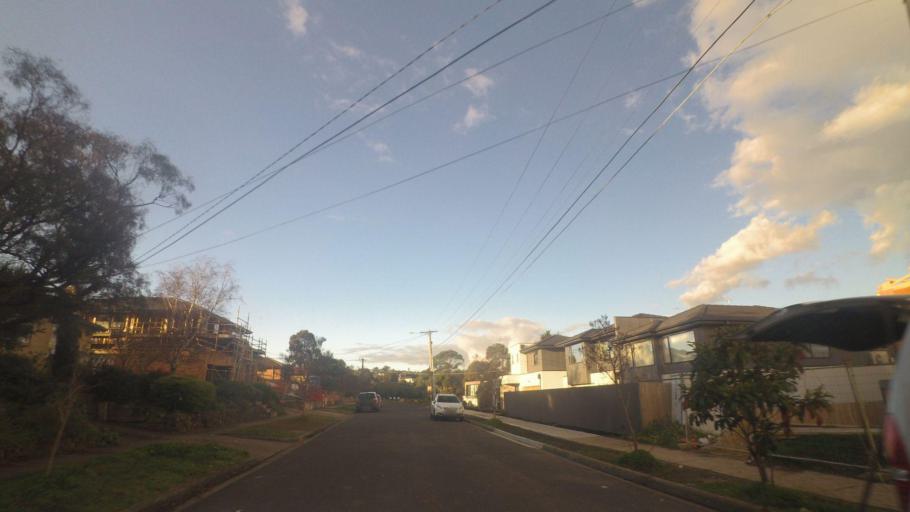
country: AU
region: Victoria
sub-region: Boroondara
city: Balwyn North
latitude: -37.7759
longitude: 145.0968
